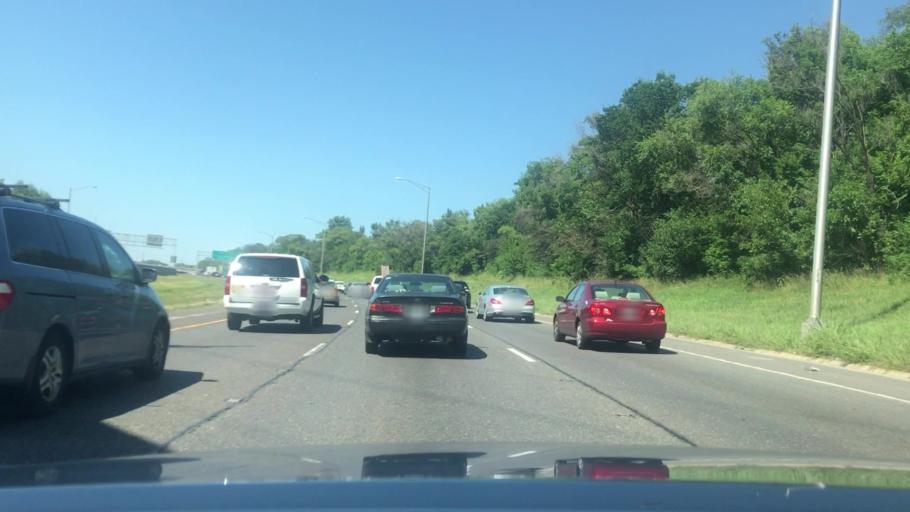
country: US
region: Illinois
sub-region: Cook County
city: Calumet Park
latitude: 41.7007
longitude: -87.6530
